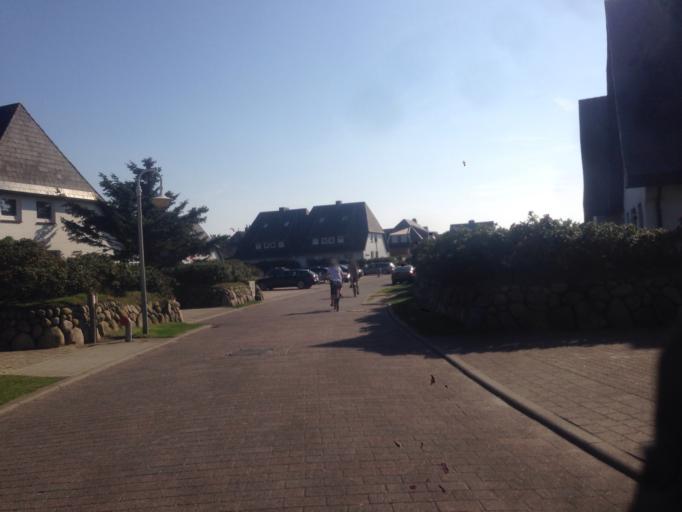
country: DE
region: Schleswig-Holstein
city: Westerland
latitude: 54.9326
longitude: 8.3148
